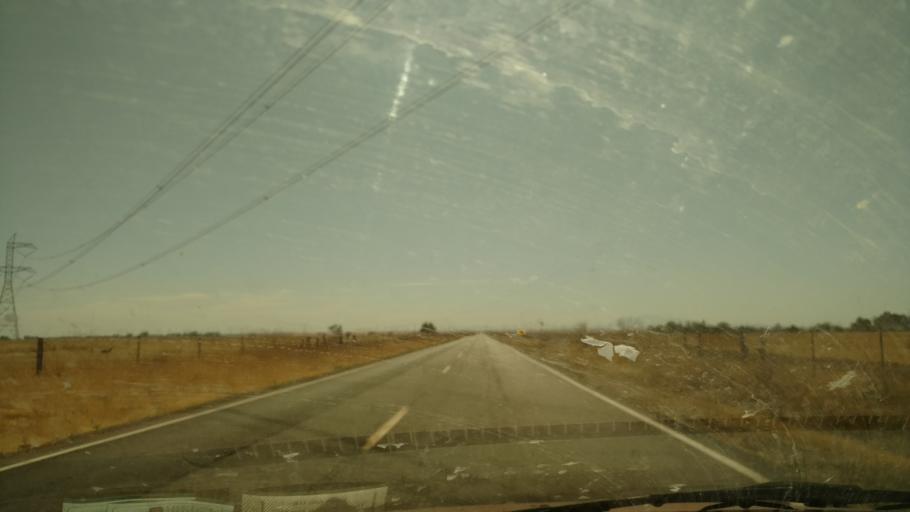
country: US
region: California
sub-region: Solano County
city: Rio Vista
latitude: 38.2532
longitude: -121.8056
